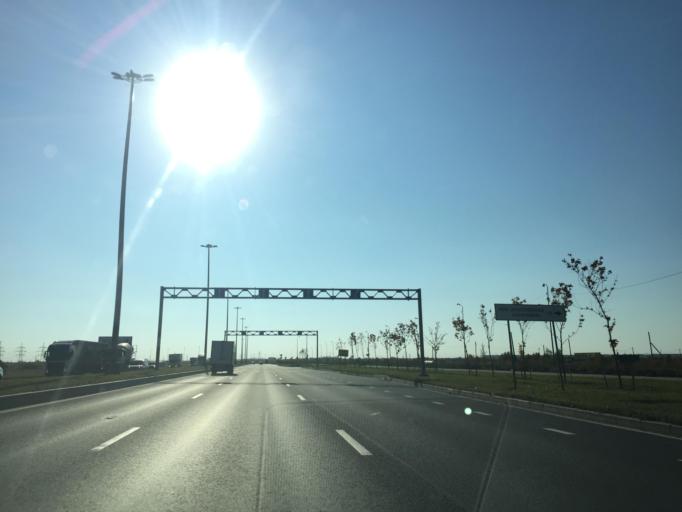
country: RU
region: St.-Petersburg
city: Petro-Slavyanka
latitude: 59.7727
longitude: 30.4995
